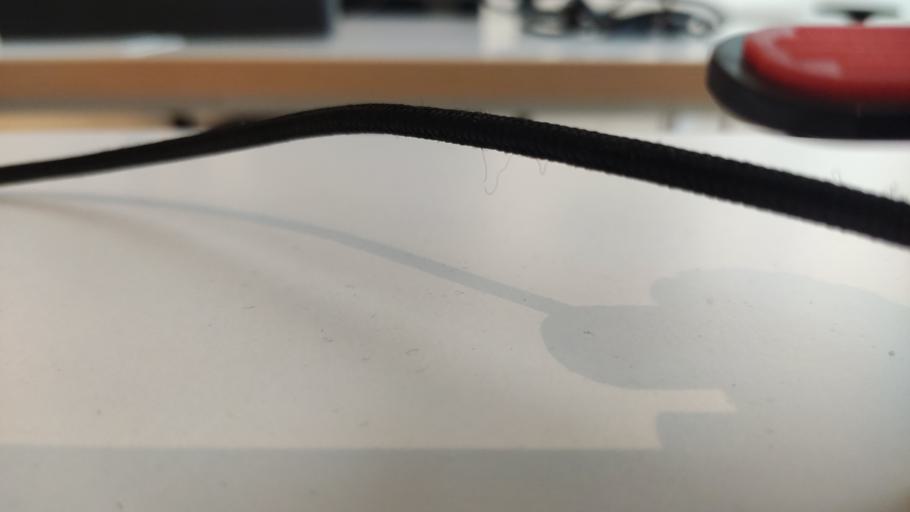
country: RU
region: Moskovskaya
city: Shevlyakovo
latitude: 56.3920
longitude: 36.8628
